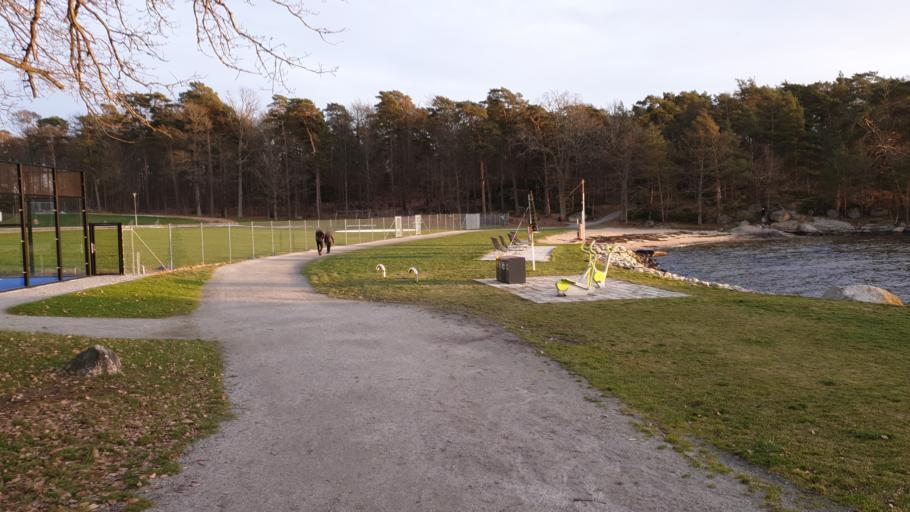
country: SE
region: Blekinge
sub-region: Karlshamns Kommun
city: Karlshamn
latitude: 56.1613
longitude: 14.8780
